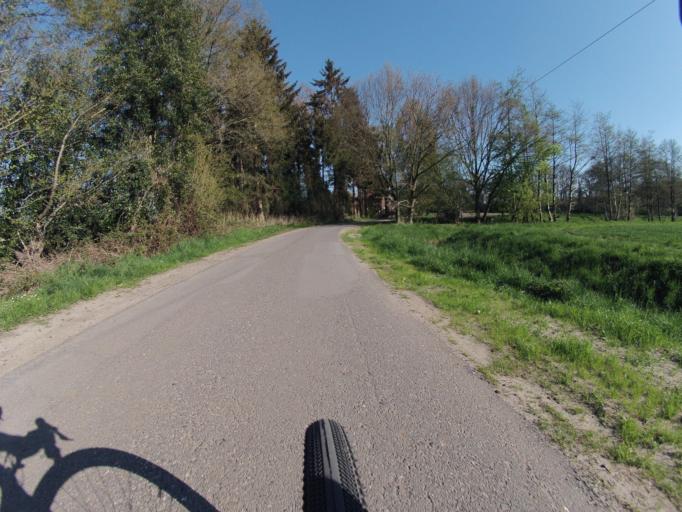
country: DE
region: Lower Saxony
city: Quendorf
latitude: 52.3421
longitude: 7.1805
